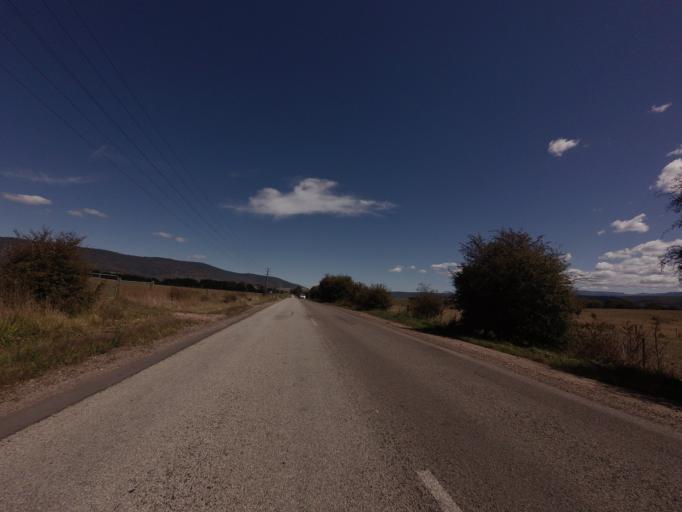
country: AU
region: Tasmania
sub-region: Break O'Day
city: St Helens
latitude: -41.6243
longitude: 147.9959
